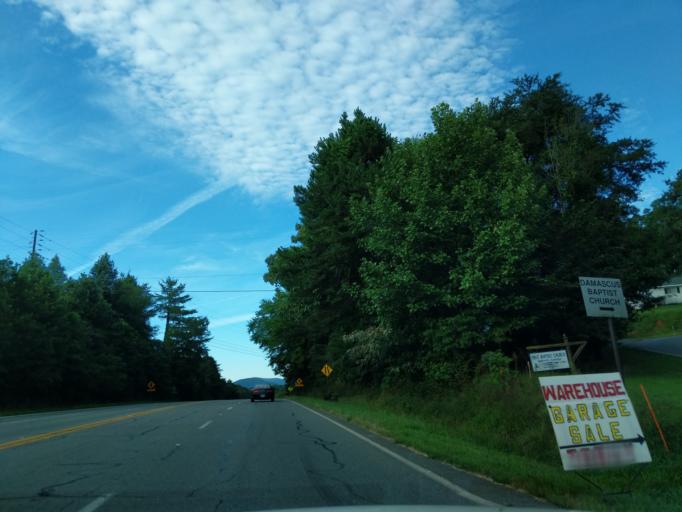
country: US
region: Georgia
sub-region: Fannin County
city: McCaysville
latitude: 34.9296
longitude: -84.3737
